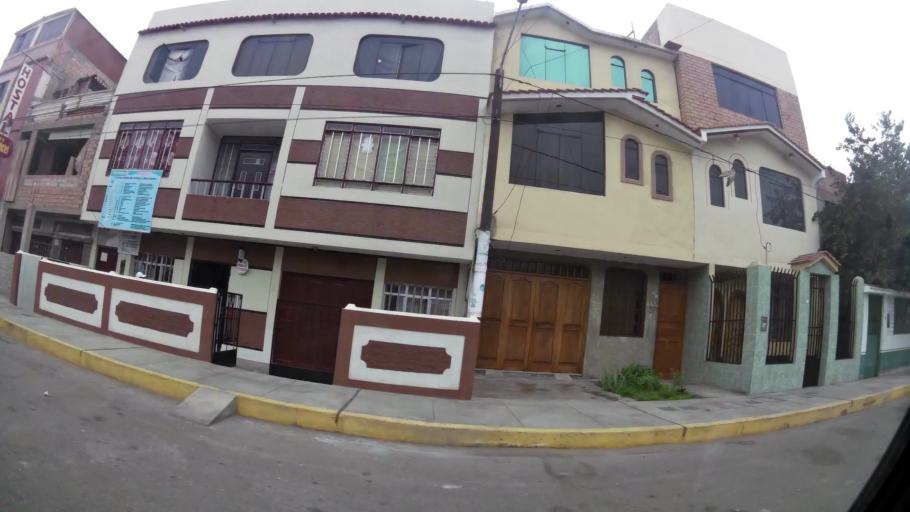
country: PE
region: Ancash
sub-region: Provincia de Santa
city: Chimbote
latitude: -9.0711
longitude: -78.5975
